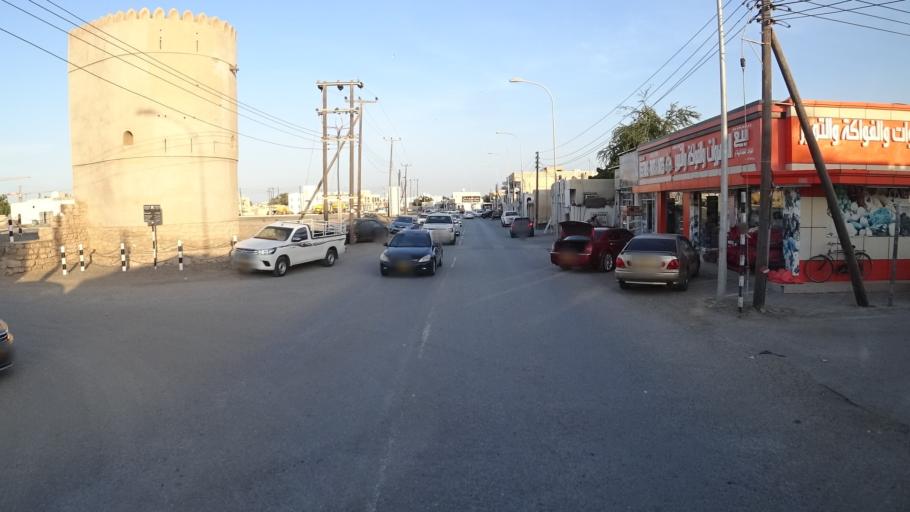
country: OM
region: Al Batinah
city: Barka'
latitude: 23.7072
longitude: 57.8946
